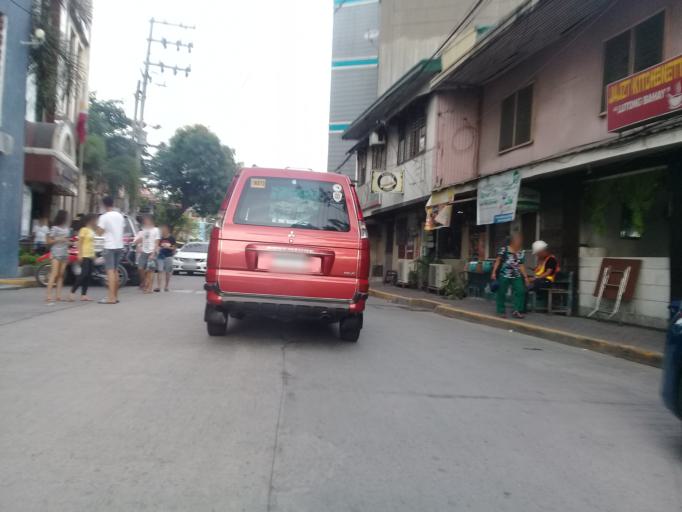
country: PH
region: Metro Manila
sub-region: Mandaluyong
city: Mandaluyong City
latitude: 14.5755
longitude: 121.0168
